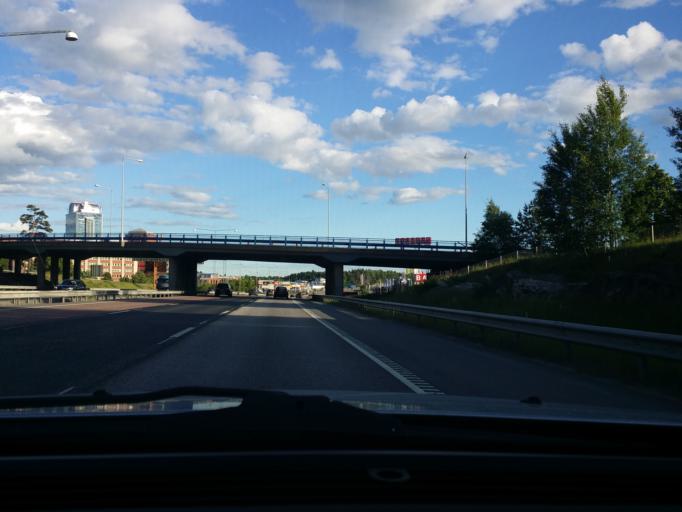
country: SE
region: Stockholm
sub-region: Upplands Vasby Kommun
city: Upplands Vaesby
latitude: 59.5042
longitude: 17.9248
